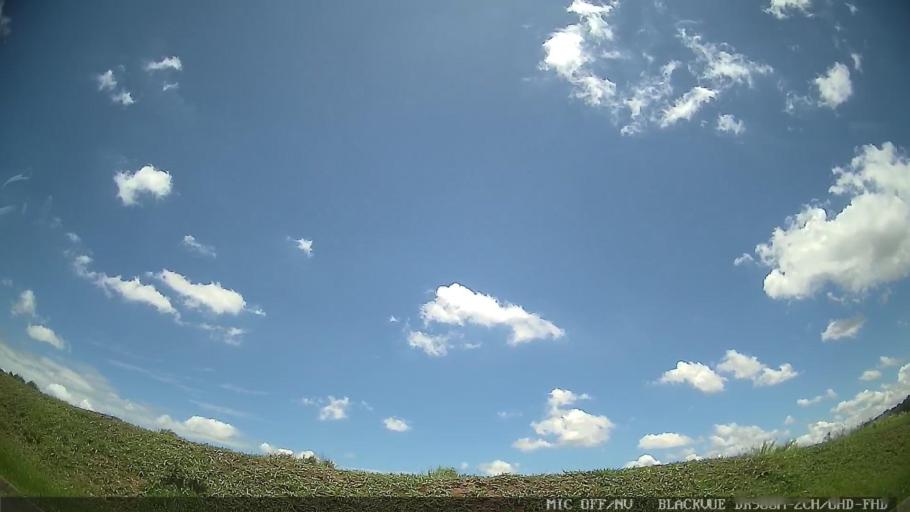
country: BR
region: Sao Paulo
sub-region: Valinhos
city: Valinhos
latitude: -22.9662
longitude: -47.0266
